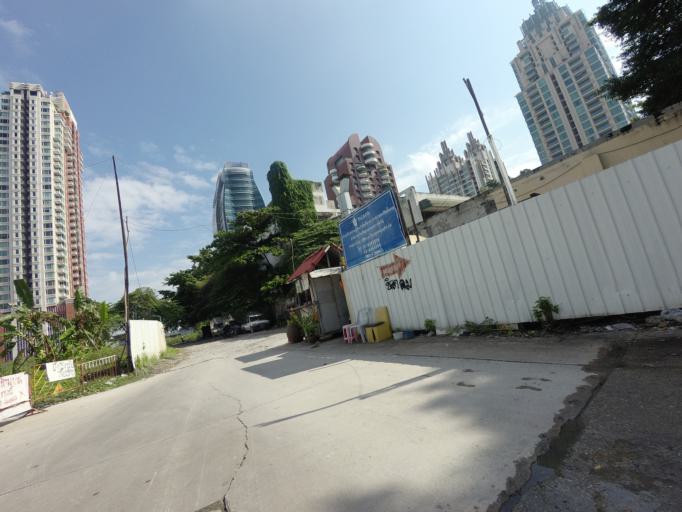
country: TH
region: Bangkok
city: Ratchathewi
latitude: 13.7480
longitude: 100.5368
